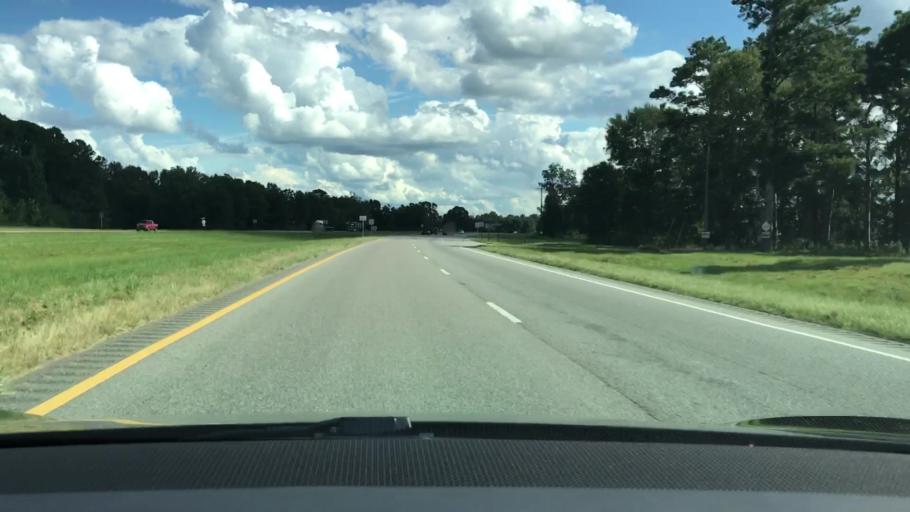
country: US
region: Alabama
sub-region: Montgomery County
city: Taylor
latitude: 32.0420
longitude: -86.0350
